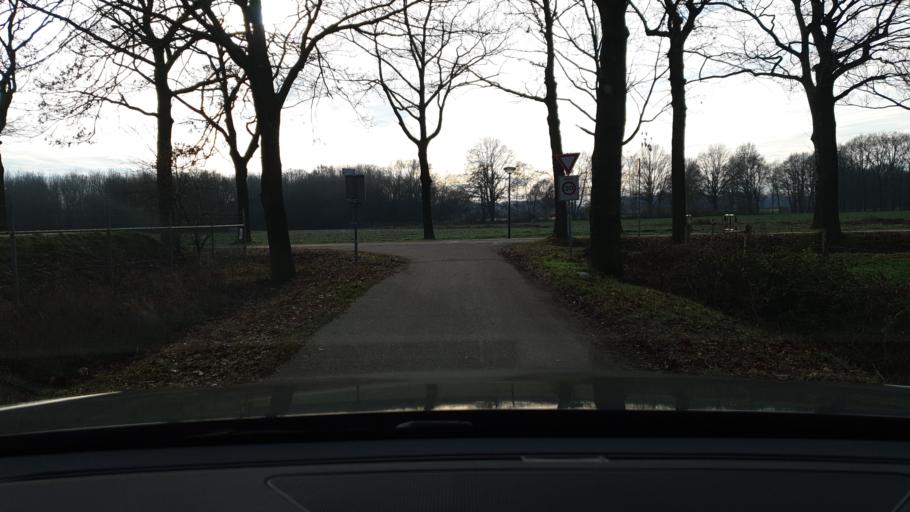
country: NL
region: North Brabant
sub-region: Gemeente Eindhoven
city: Muschberg en Geestenberg
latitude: 51.4222
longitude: 5.5298
